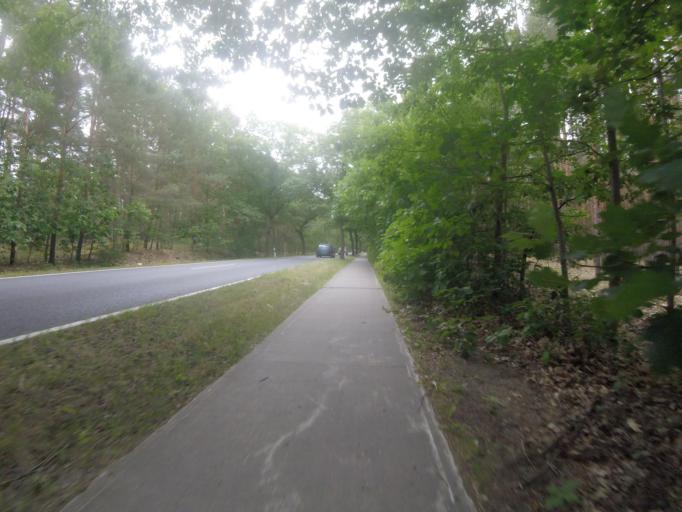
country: DE
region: Brandenburg
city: Bestensee
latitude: 52.2567
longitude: 13.6323
